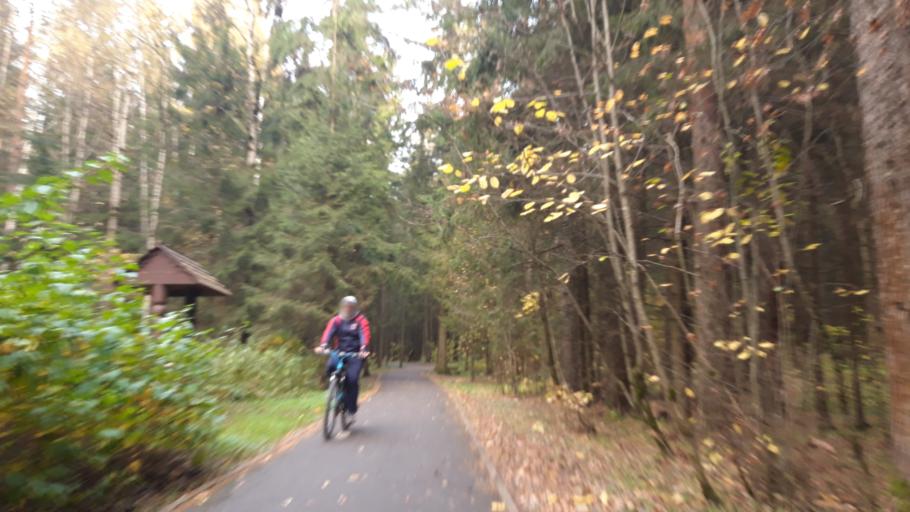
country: RU
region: Moskovskaya
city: Alabushevo
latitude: 55.9998
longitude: 37.1643
